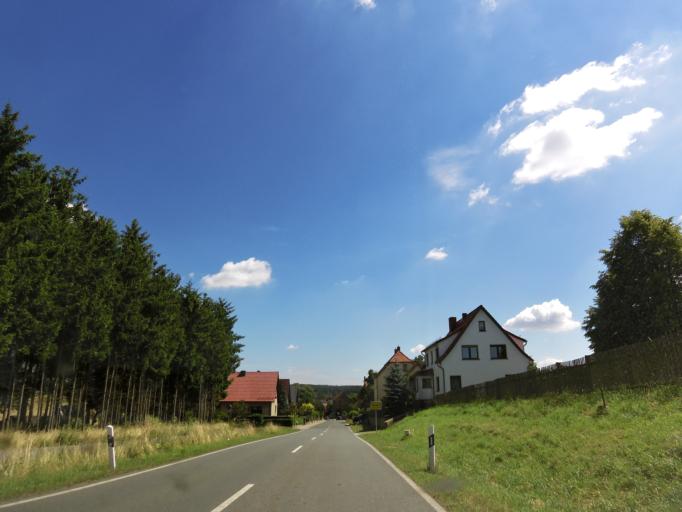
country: DE
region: Thuringia
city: Reichenbach
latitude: 50.8861
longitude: 11.8880
